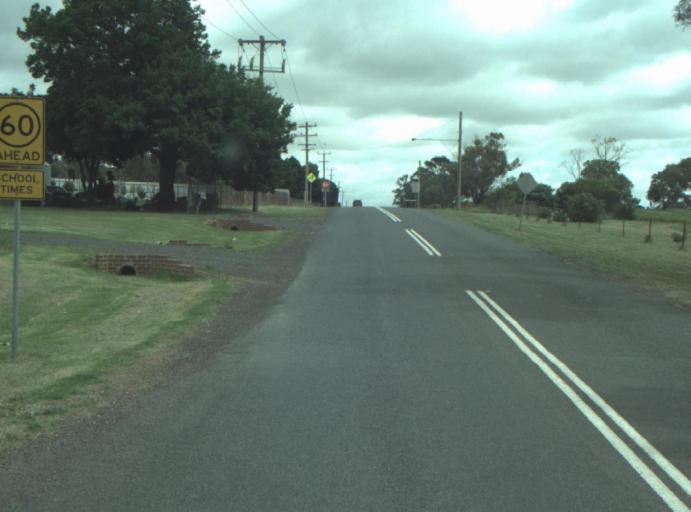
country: AU
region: Victoria
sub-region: Greater Geelong
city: Bell Post Hill
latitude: -38.0703
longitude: 144.3299
